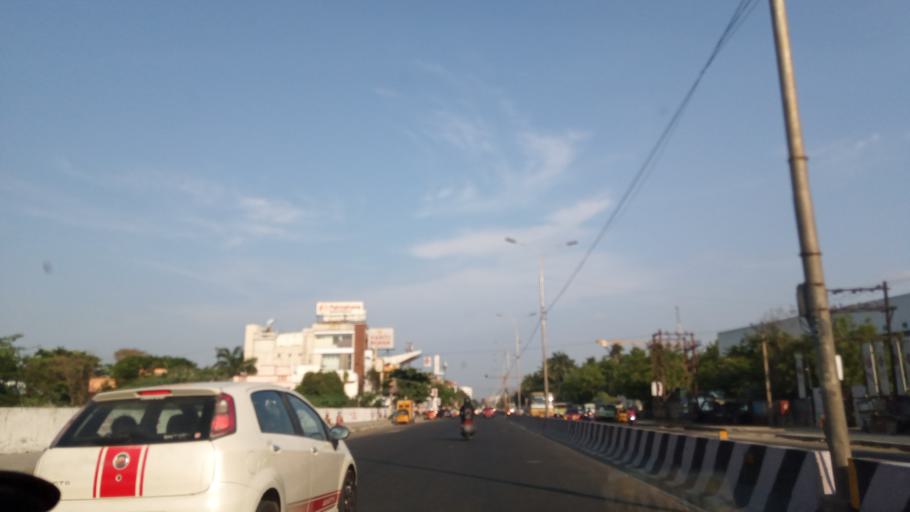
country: IN
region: Tamil Nadu
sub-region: Kancheepuram
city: Manappakkam
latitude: 13.0267
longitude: 80.1736
